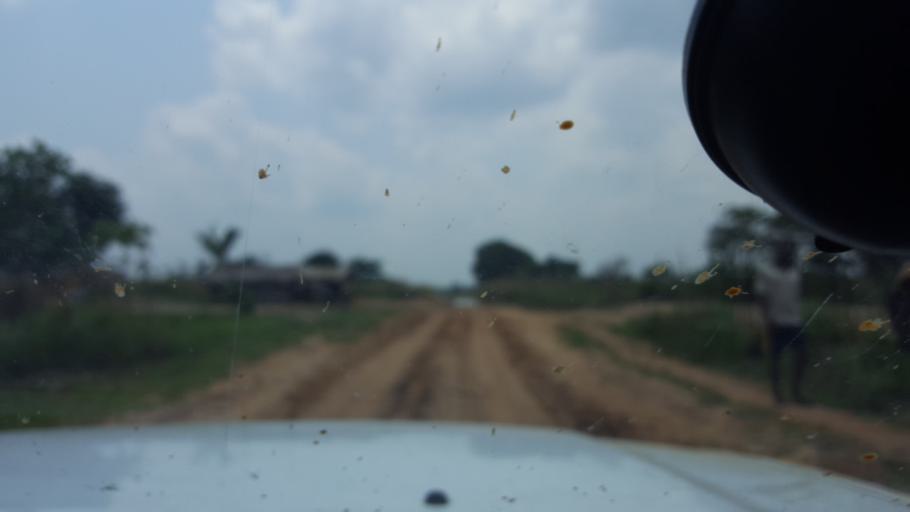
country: CD
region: Bandundu
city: Mushie
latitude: -3.7483
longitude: 16.6489
